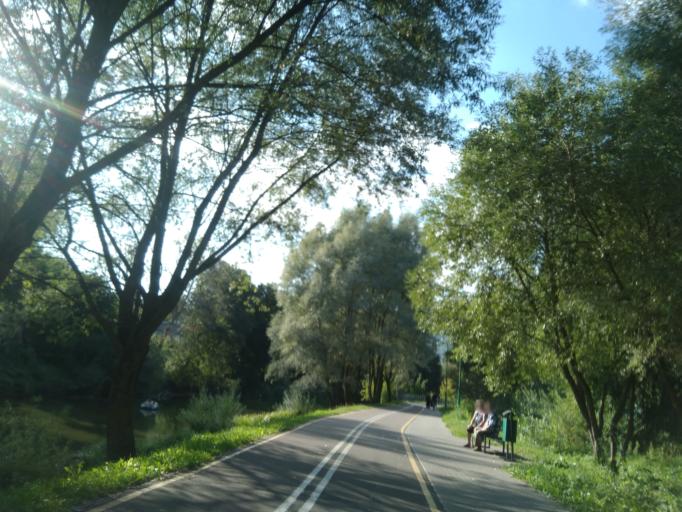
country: BY
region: Minsk
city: Minsk
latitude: 53.8714
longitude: 27.5848
